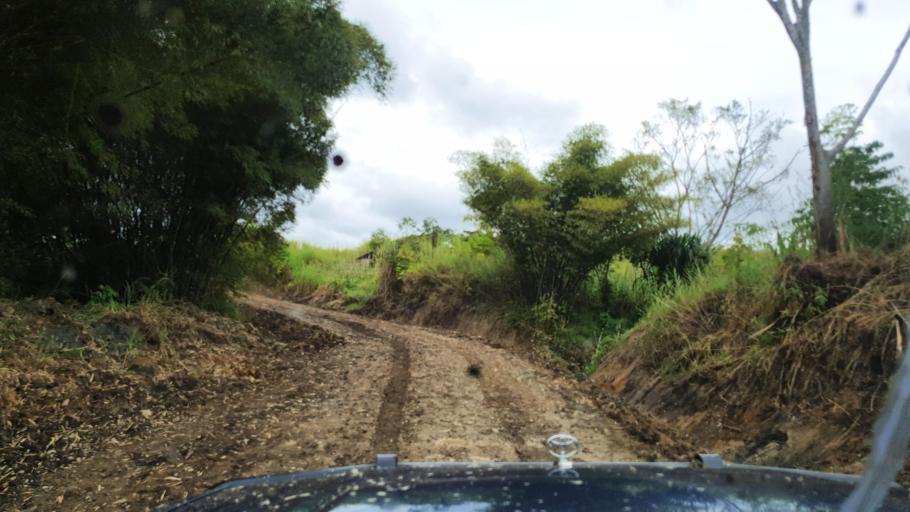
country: PG
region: Jiwaka
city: Minj
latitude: -5.9290
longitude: 144.7428
